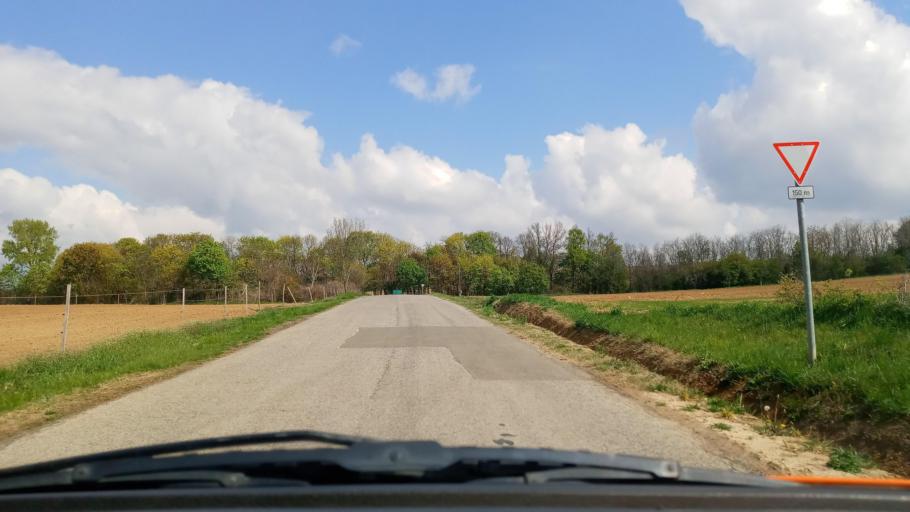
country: HU
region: Baranya
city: Pecsvarad
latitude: 46.1082
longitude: 18.4864
